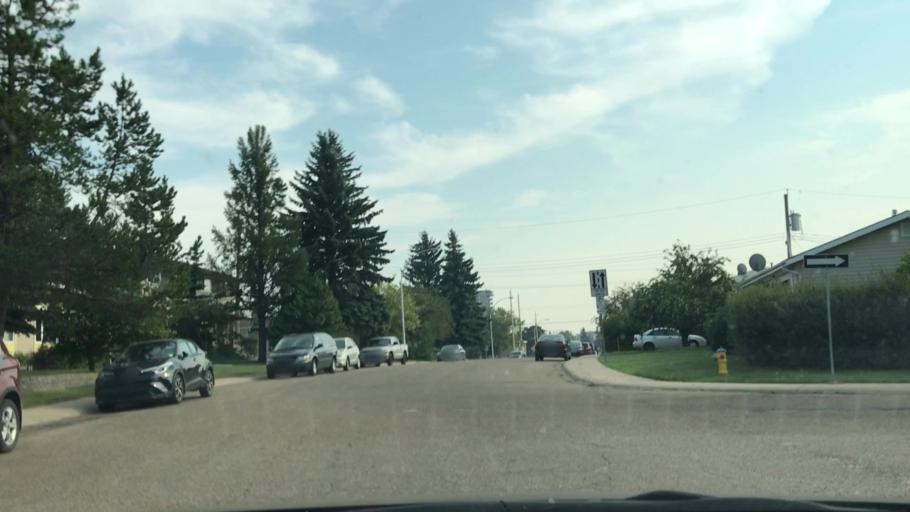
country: CA
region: Alberta
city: Edmonton
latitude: 53.4896
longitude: -113.5080
